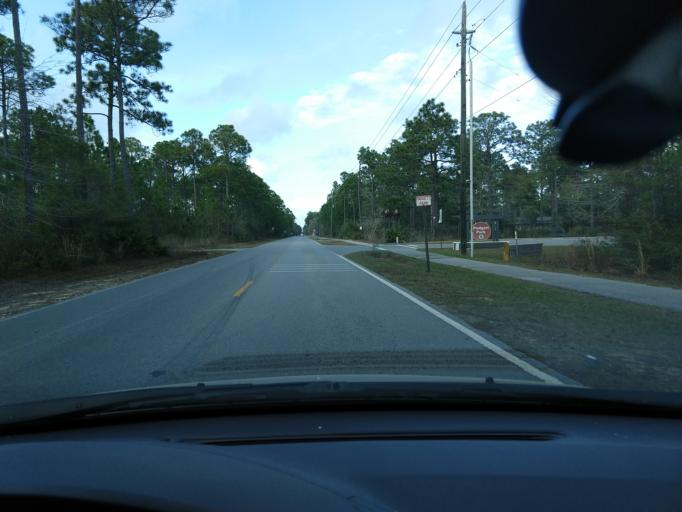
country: US
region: Florida
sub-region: Walton County
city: Seaside
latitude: 30.3788
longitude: -86.1871
